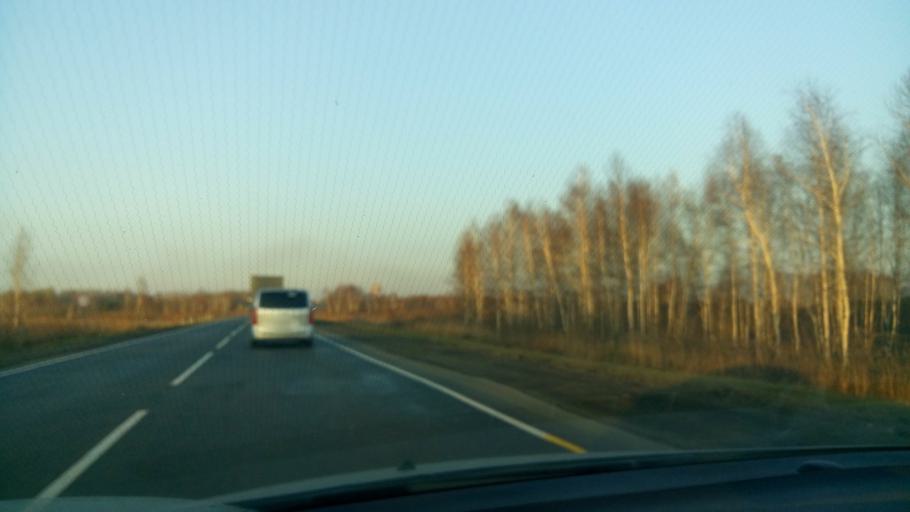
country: RU
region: Sverdlovsk
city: Yelanskiy
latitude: 56.8042
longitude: 62.5215
